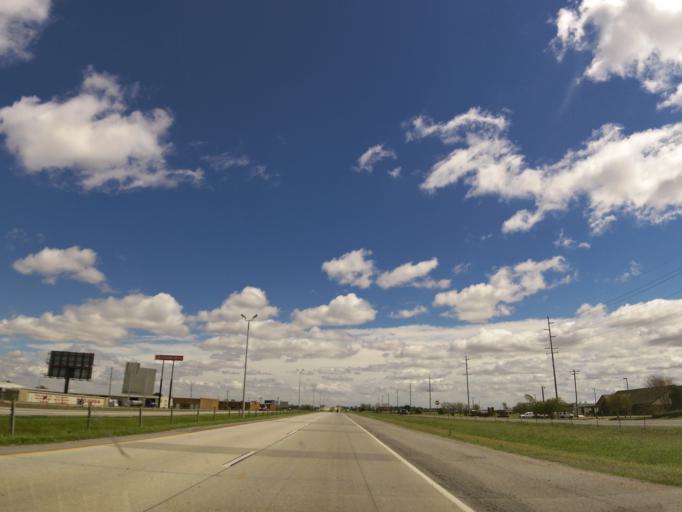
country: US
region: Arkansas
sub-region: Craighead County
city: Jonesboro
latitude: 35.8069
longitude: -90.6497
